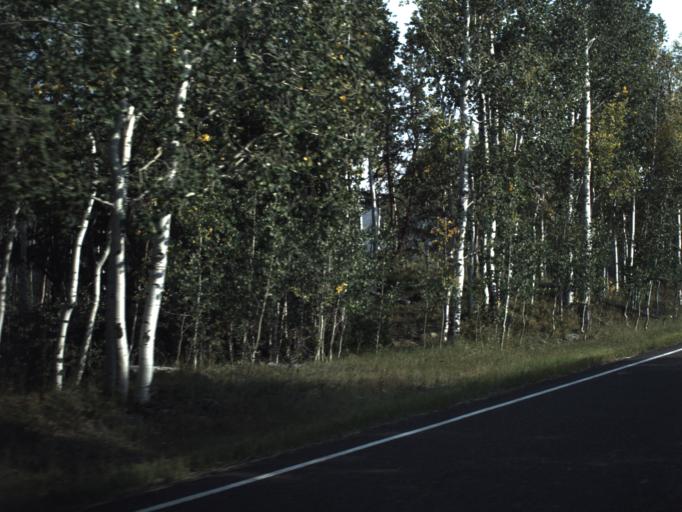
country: US
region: Wyoming
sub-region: Uinta County
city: Evanston
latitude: 40.8445
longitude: -110.8473
